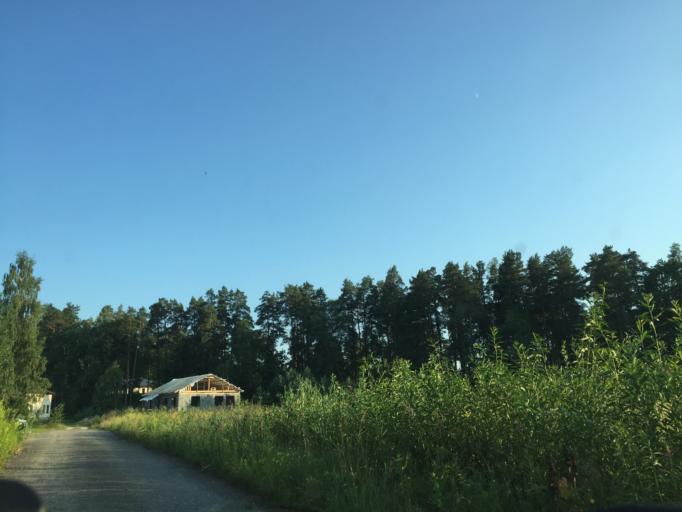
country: LV
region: Garkalne
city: Garkalne
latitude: 56.9804
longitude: 24.3794
